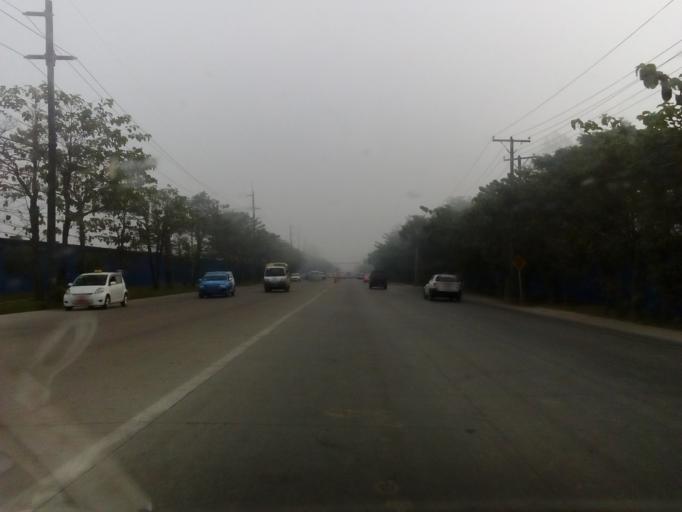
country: MM
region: Yangon
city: Yangon
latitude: 16.8139
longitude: 96.1884
